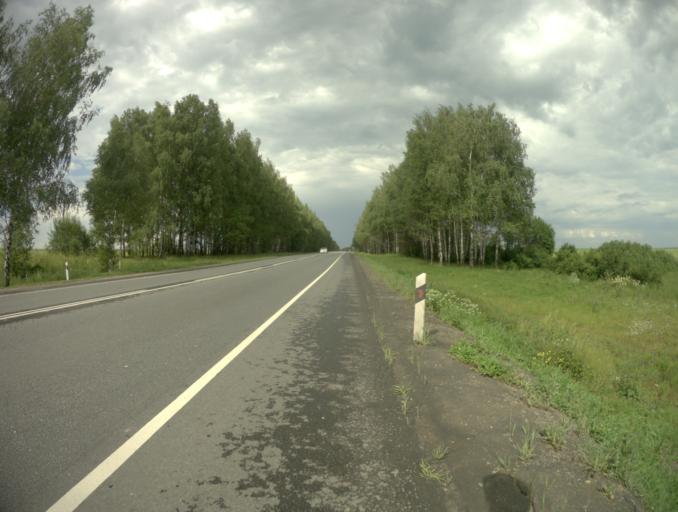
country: RU
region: Vladimir
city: Bogolyubovo
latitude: 56.2529
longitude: 40.4598
